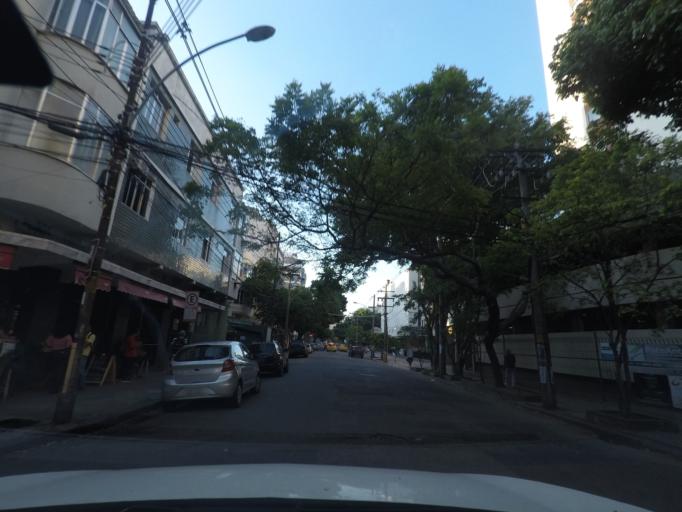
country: BR
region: Rio de Janeiro
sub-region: Rio De Janeiro
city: Rio de Janeiro
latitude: -22.9173
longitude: -43.2177
